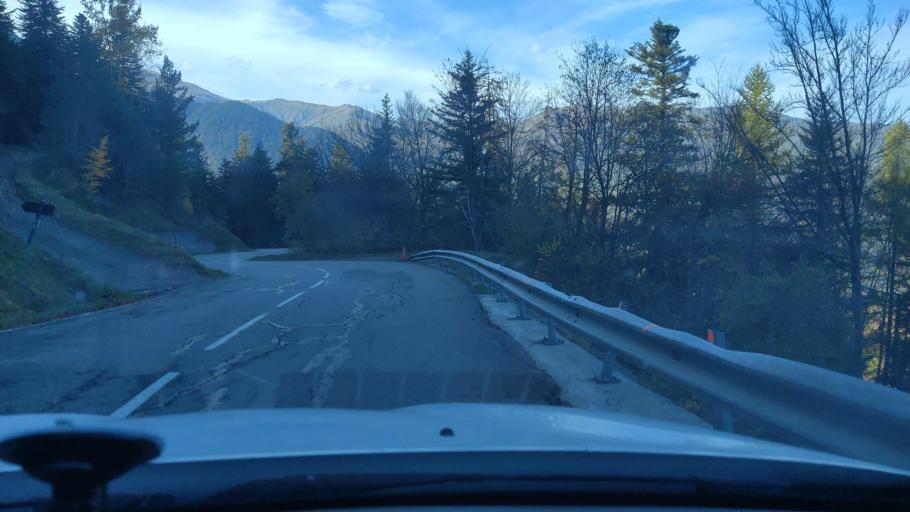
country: FR
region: Rhone-Alpes
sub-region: Departement de la Savoie
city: Villargondran
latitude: 45.2249
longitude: 6.3277
